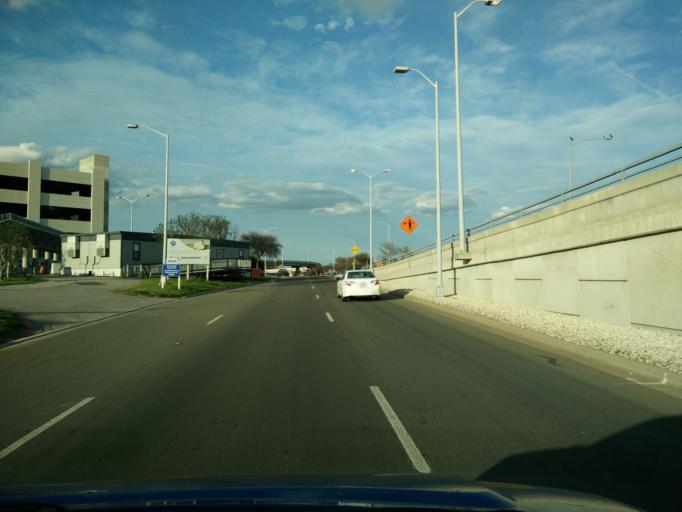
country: US
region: Texas
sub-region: Travis County
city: Hornsby Bend
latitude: 30.2034
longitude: -97.6646
